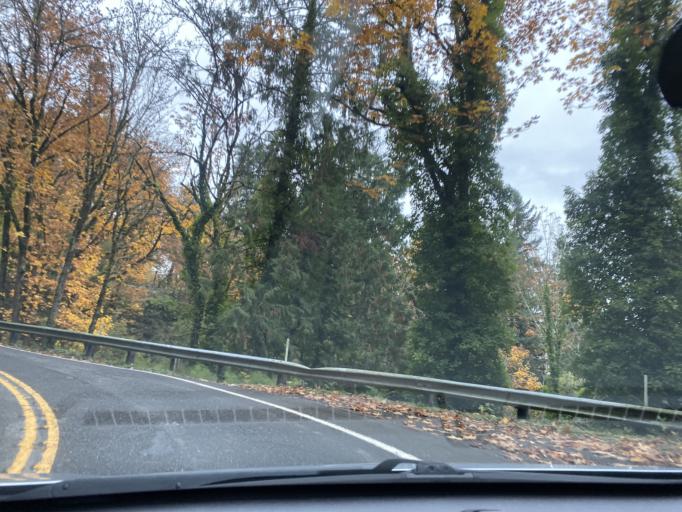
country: US
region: Washington
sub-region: King County
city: Lea Hill
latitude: 47.3001
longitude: -122.1716
